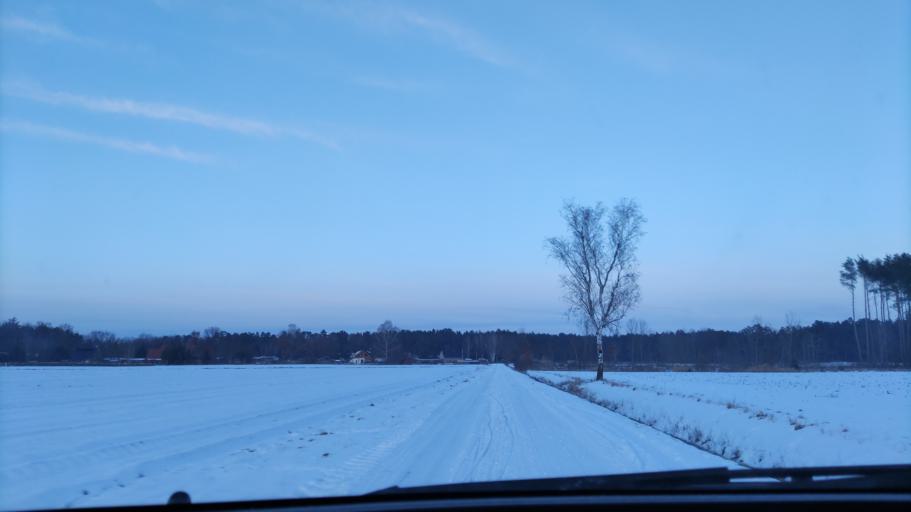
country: DE
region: Lower Saxony
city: Bleckede
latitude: 53.2903
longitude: 10.6852
